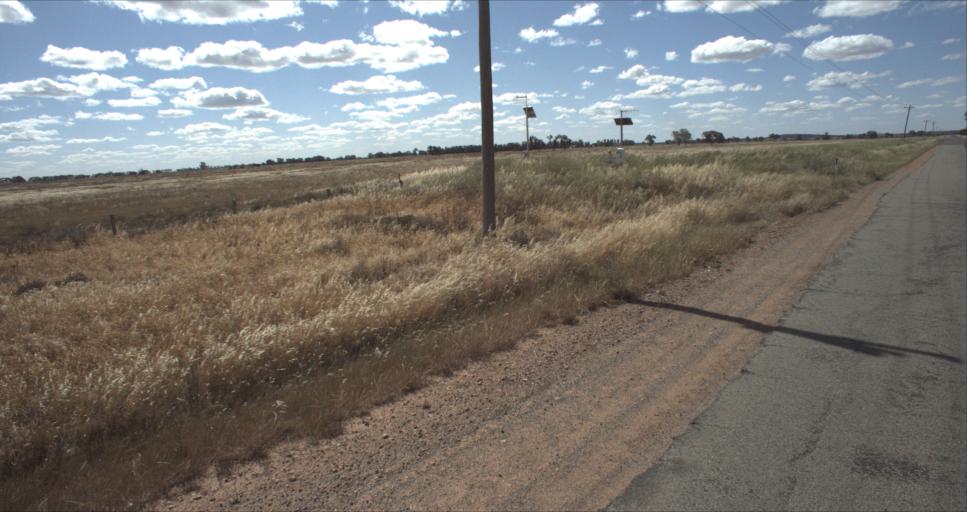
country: AU
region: New South Wales
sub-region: Leeton
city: Leeton
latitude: -34.4751
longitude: 146.2502
